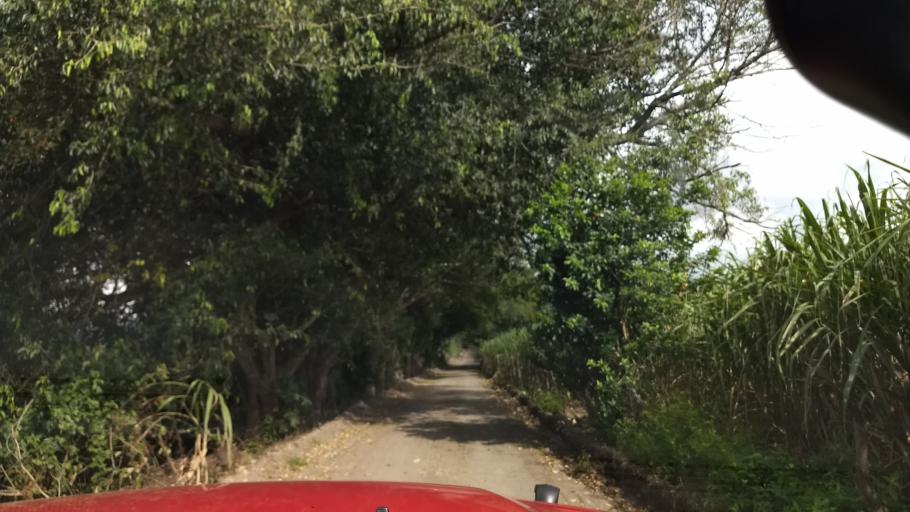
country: MX
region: Colima
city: Suchitlan
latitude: 19.4616
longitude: -103.7567
